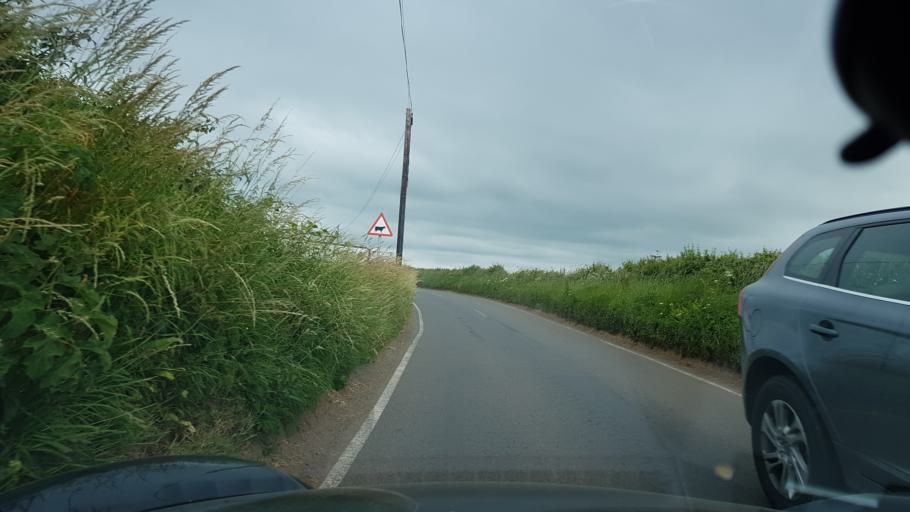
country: GB
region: Wales
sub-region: Pembrokeshire
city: Herbrandston
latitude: 51.7534
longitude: -5.1195
